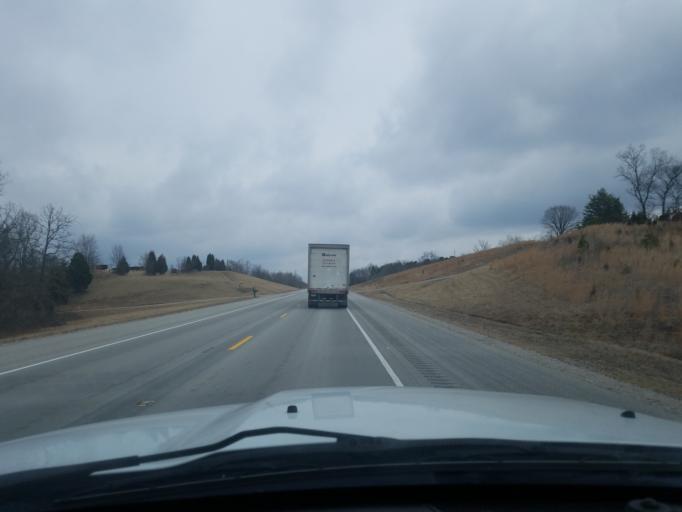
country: US
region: Indiana
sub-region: Perry County
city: Tell City
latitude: 38.1169
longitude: -86.6080
